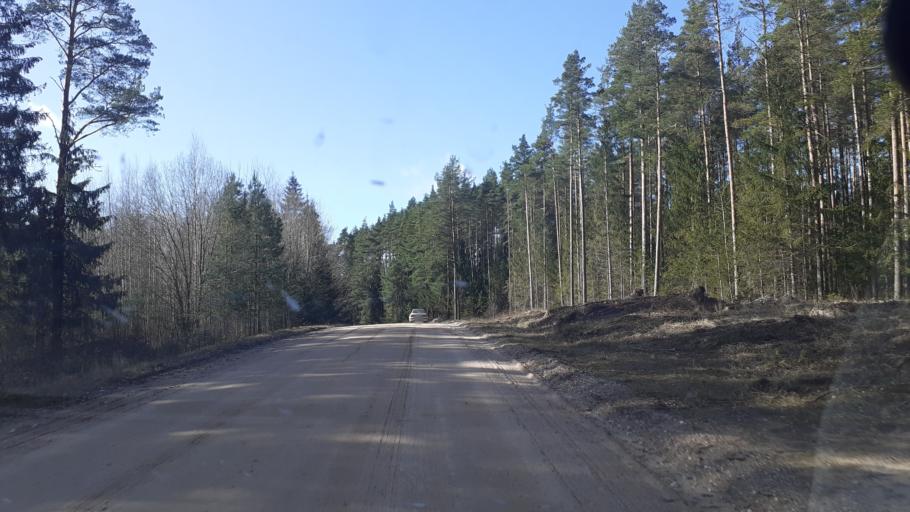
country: LV
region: Kuldigas Rajons
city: Kuldiga
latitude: 56.9128
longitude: 22.0879
